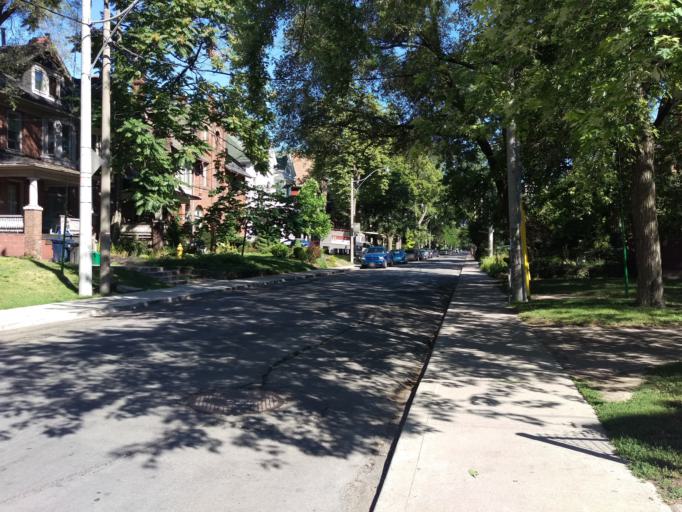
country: CA
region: Ontario
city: Toronto
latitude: 43.6664
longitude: -79.4076
